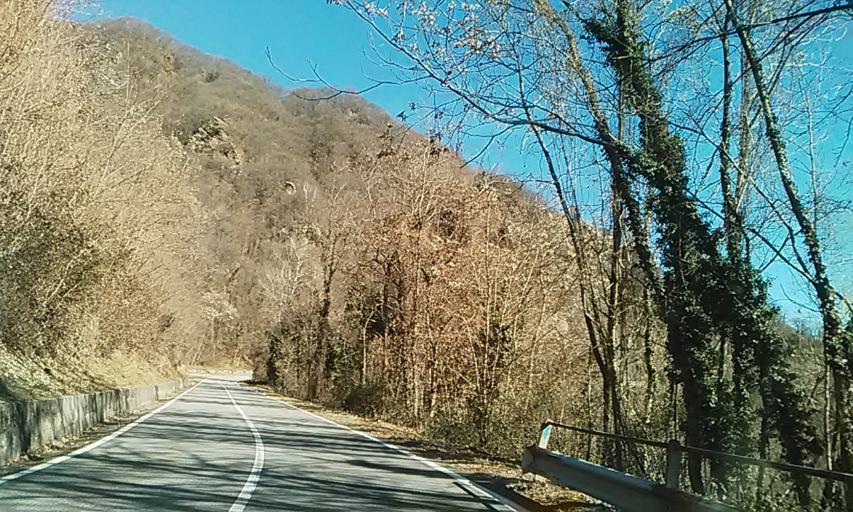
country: IT
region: Piedmont
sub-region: Provincia di Vercelli
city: Civiasco
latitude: 45.8025
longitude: 8.2802
